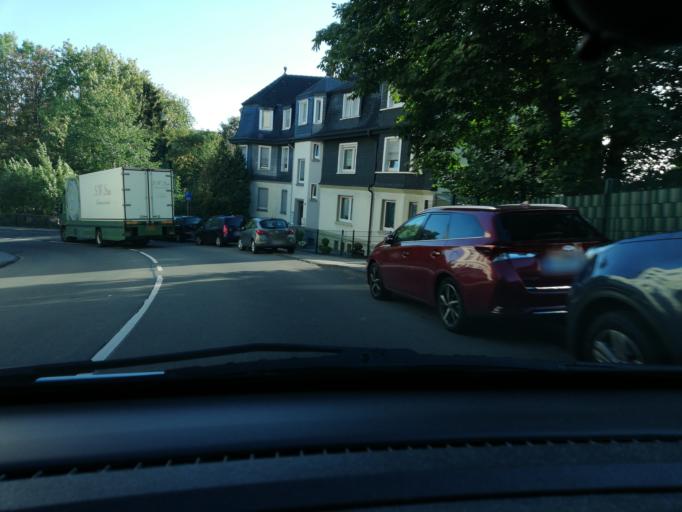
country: DE
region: North Rhine-Westphalia
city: Gevelsberg
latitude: 51.3243
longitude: 7.3371
